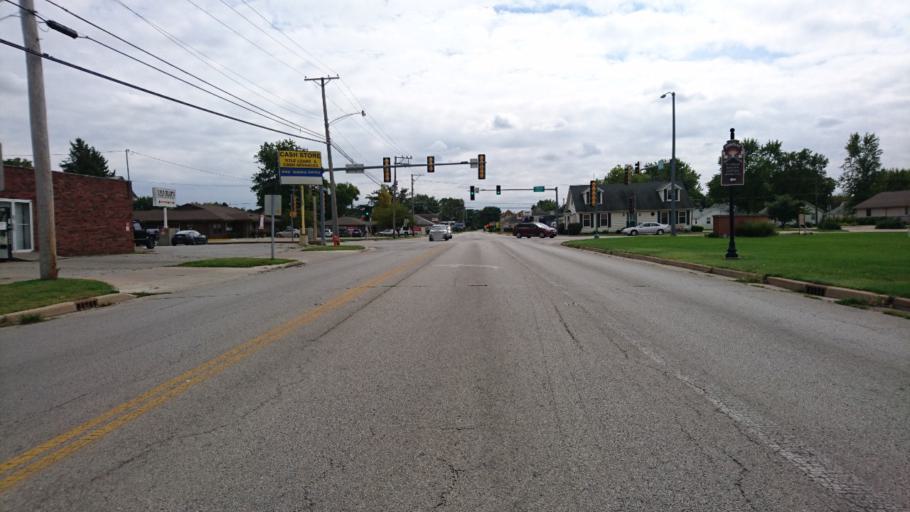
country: US
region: Illinois
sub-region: Livingston County
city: Pontiac
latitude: 40.8815
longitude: -88.6381
